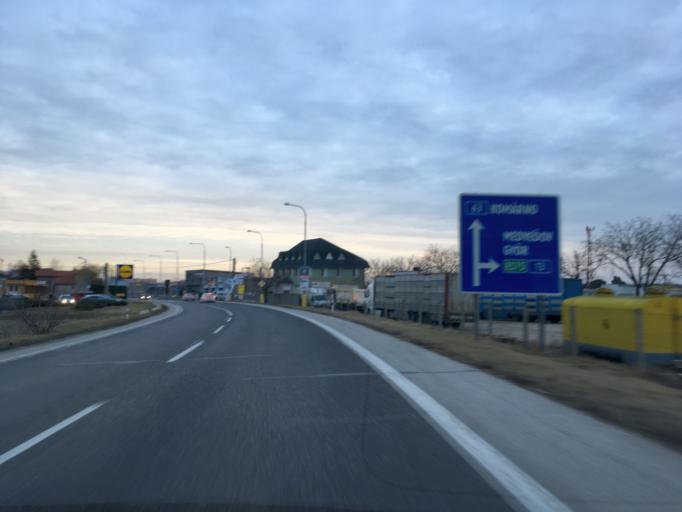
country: SK
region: Trnavsky
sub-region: Okres Dunajska Streda
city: Velky Meder
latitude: 47.8643
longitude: 17.7576
